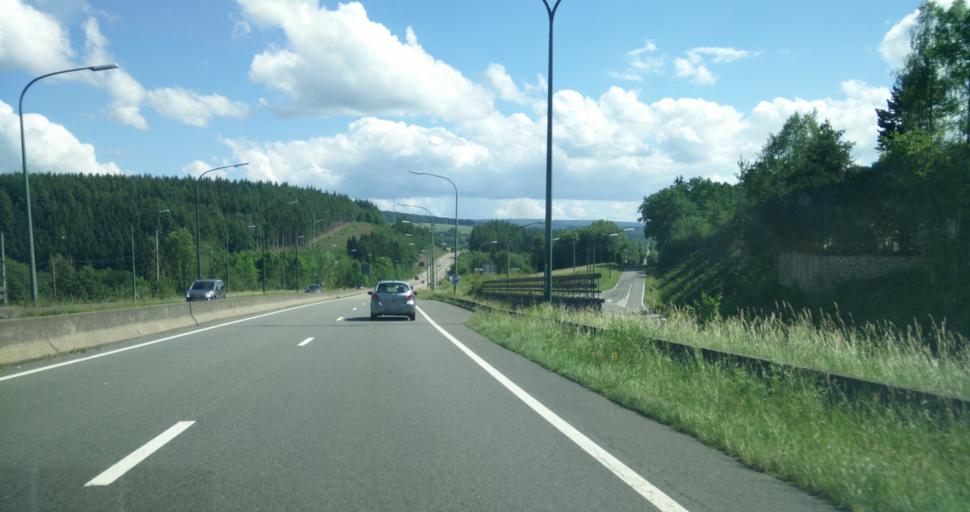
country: BE
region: Wallonia
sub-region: Province du Luxembourg
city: Marche-en-Famenne
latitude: 50.2064
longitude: 5.3675
